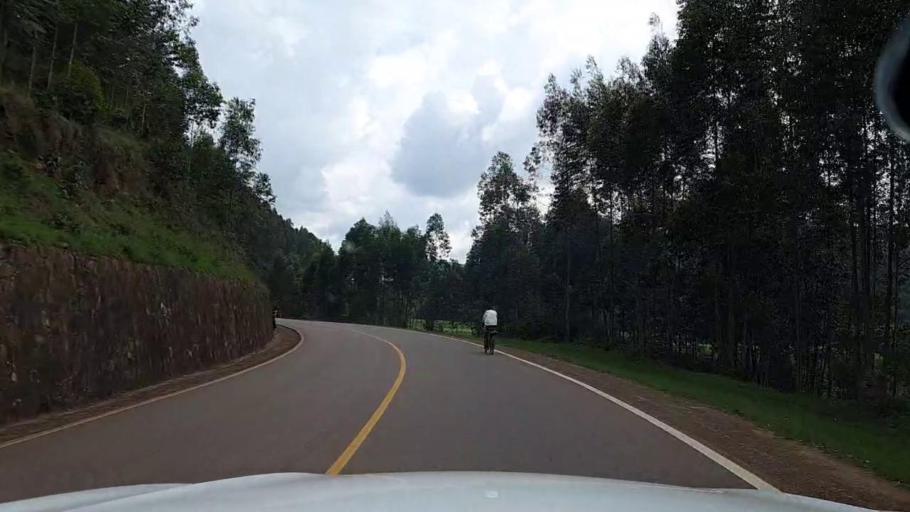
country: RW
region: Kigali
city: Kigali
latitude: -1.8198
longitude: 30.1142
